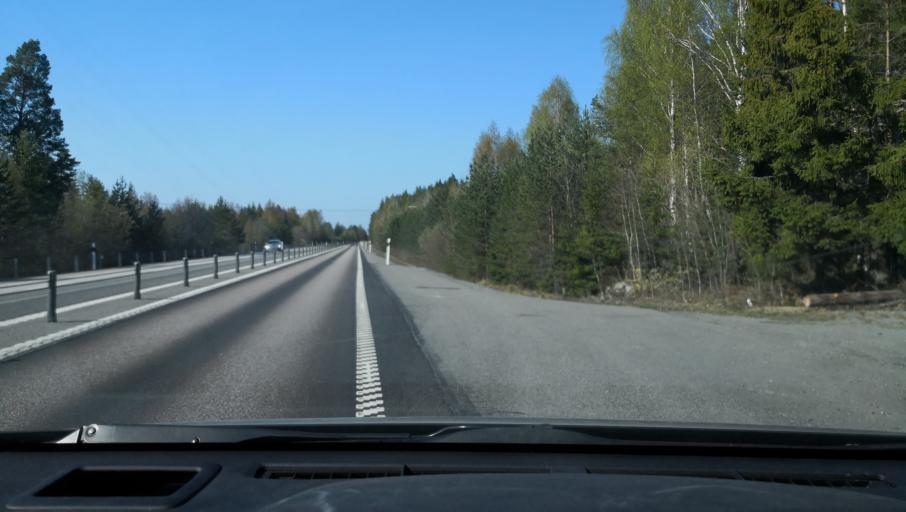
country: SE
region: Uppsala
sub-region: Heby Kommun
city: Tarnsjo
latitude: 60.2134
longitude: 16.9533
